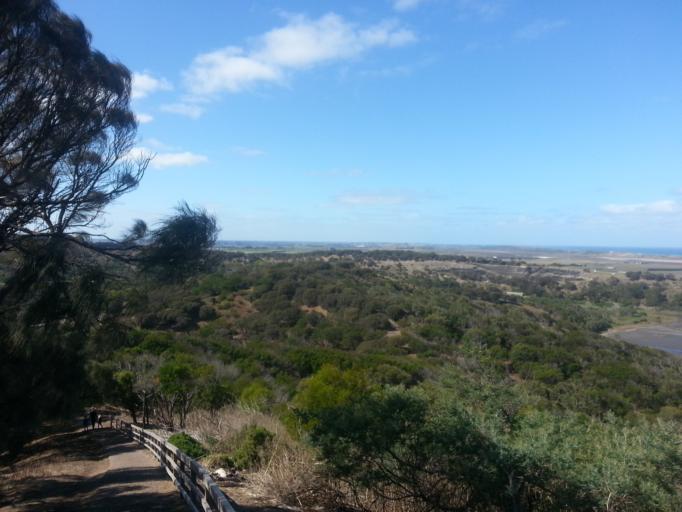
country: AU
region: Victoria
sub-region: Moyne
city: Port Fairy
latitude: -38.3214
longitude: 142.3598
